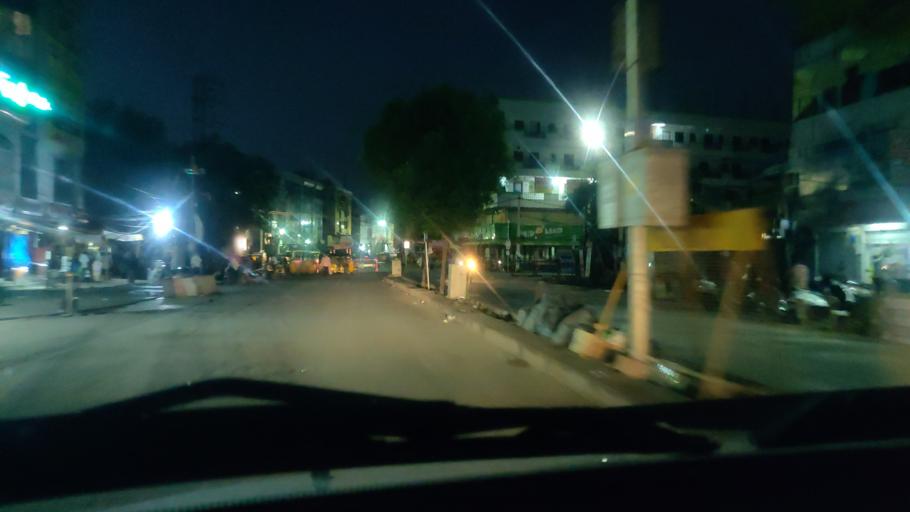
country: IN
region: Telangana
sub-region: Hyderabad
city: Hyderabad
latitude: 17.4380
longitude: 78.4483
